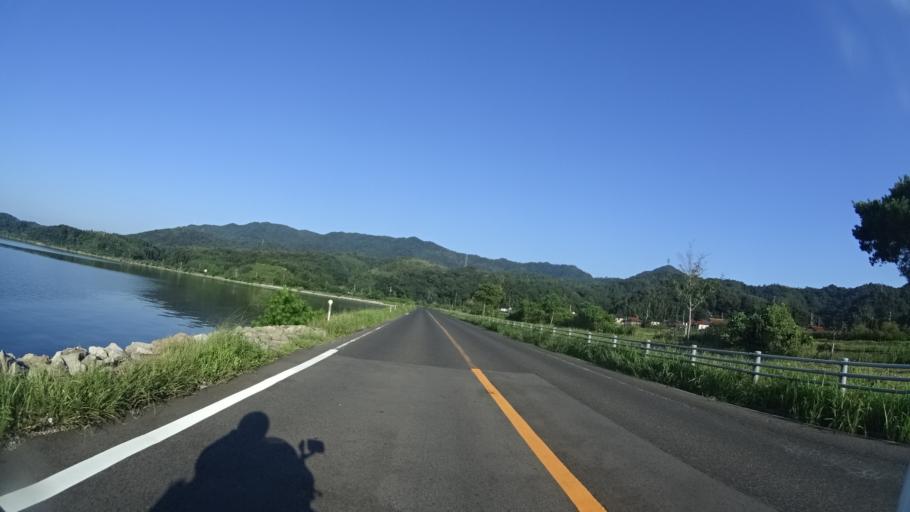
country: JP
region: Shimane
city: Sakaiminato
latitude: 35.5366
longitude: 133.1597
